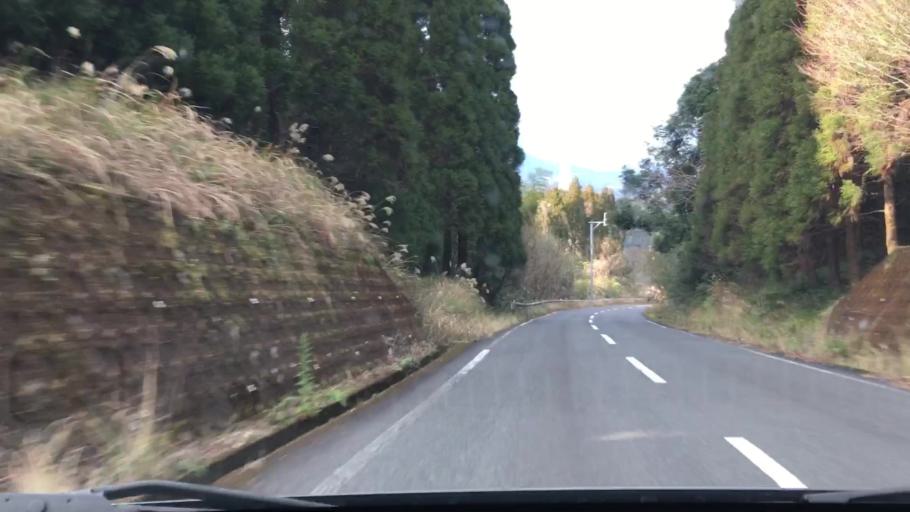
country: JP
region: Miyazaki
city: Nichinan
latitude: 31.6071
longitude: 131.3299
